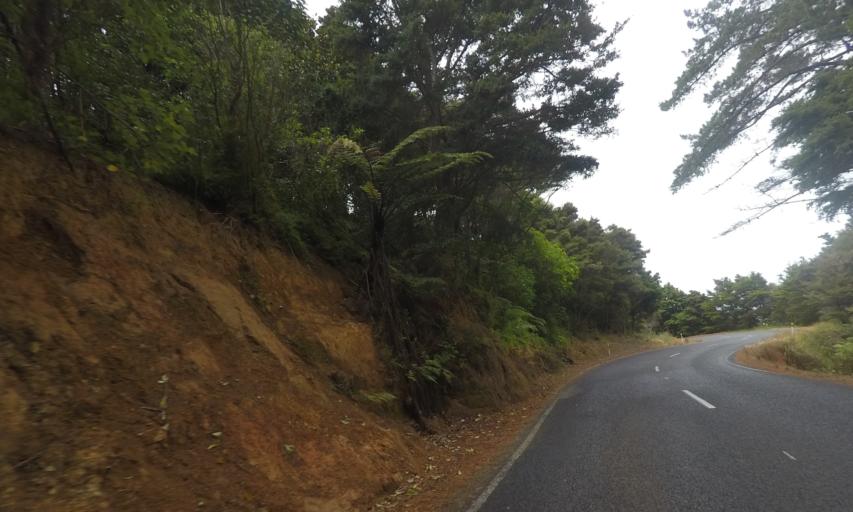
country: NZ
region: Northland
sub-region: Whangarei
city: Whangarei
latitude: -35.7626
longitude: 174.4581
